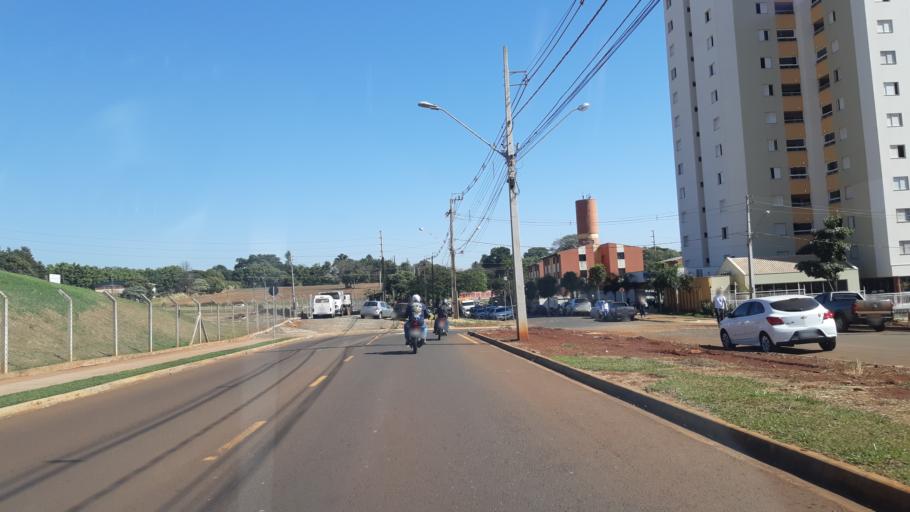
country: BR
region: Parana
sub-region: Londrina
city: Londrina
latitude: -23.3309
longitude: -51.1844
